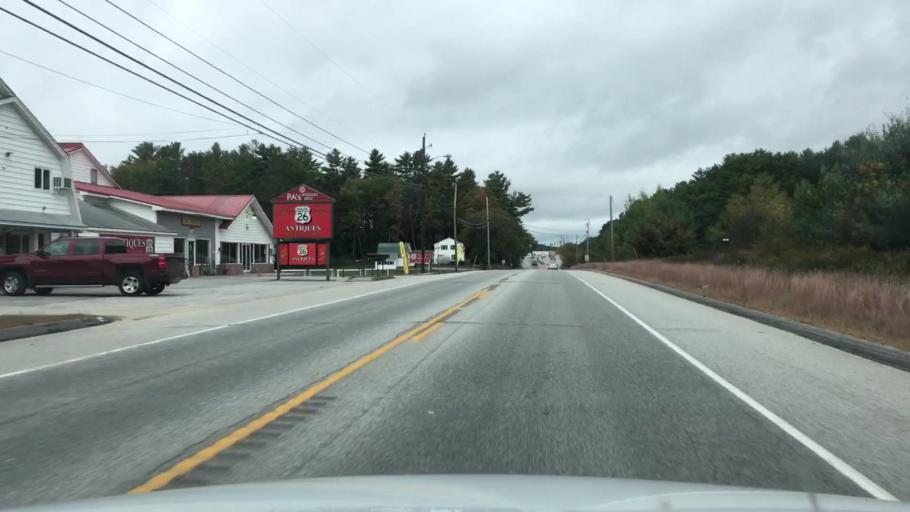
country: US
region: Maine
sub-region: Oxford County
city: Oxford
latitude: 44.1703
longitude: -70.5083
